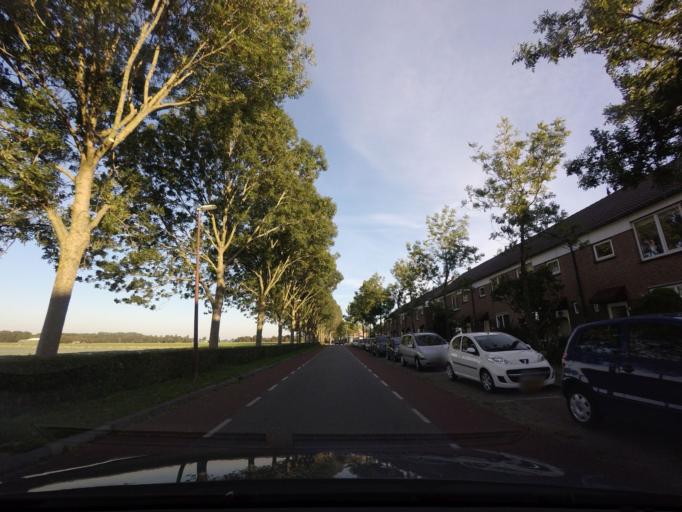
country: NL
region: North Holland
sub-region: Gemeente Langedijk
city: Broek op Langedijk
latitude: 52.6753
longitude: 4.7605
